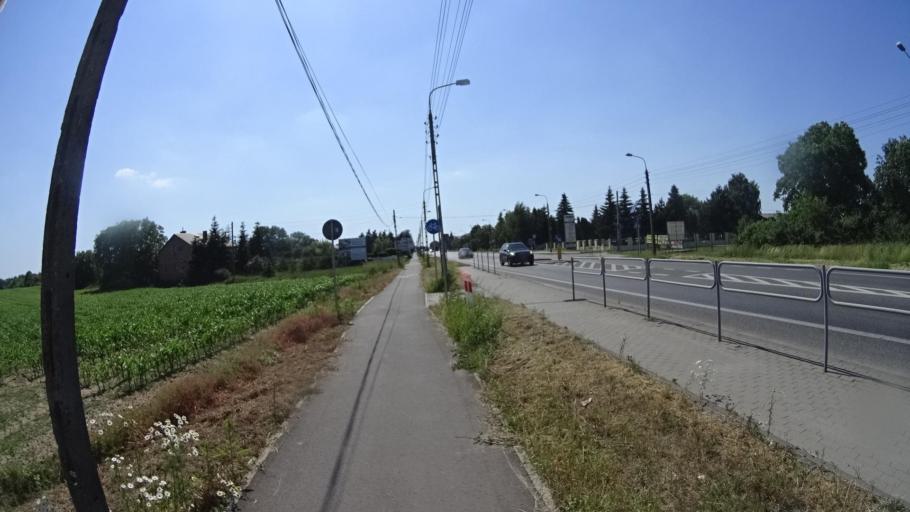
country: PL
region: Masovian Voivodeship
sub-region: Powiat warszawski zachodni
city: Blonie
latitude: 52.2028
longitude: 20.6359
